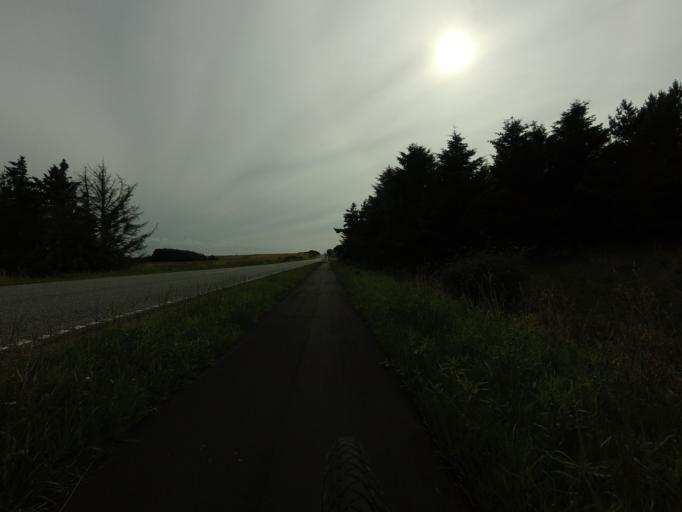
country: DK
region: North Denmark
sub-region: Hjorring Kommune
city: Vra
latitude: 57.4187
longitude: 9.8306
